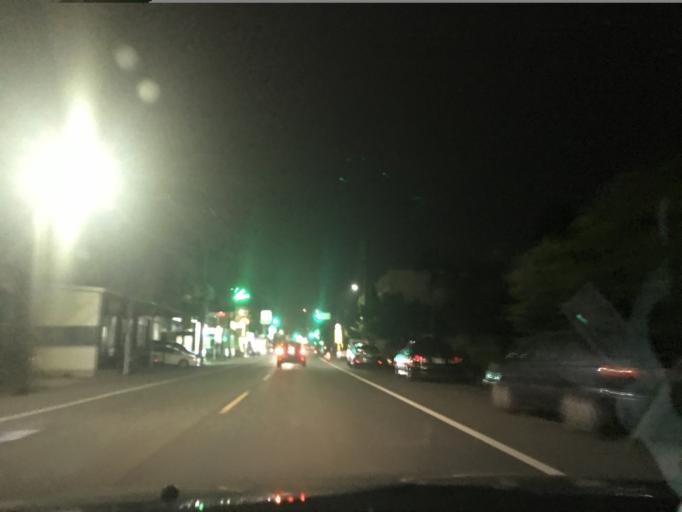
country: TW
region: Taiwan
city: Daxi
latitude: 24.9329
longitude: 121.2693
